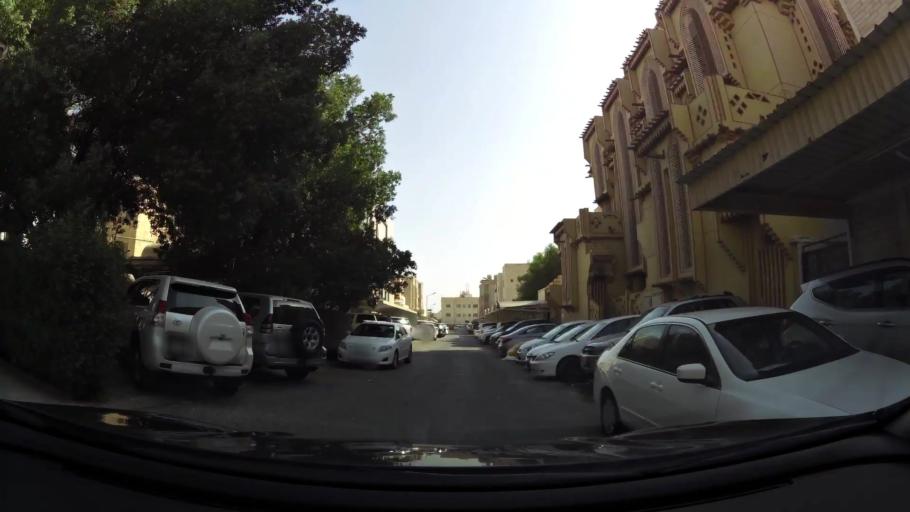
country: KW
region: Muhafazat Hawalli
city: Salwa
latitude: 29.2924
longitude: 48.0811
